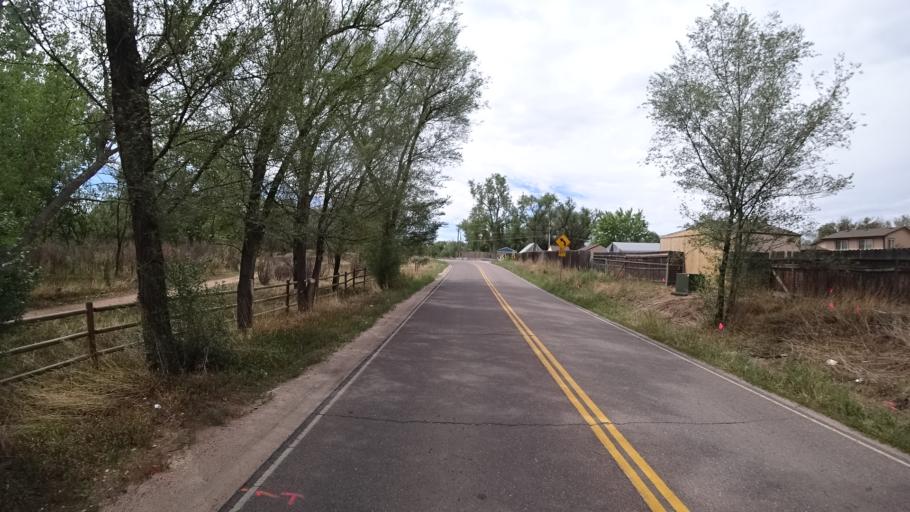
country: US
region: Colorado
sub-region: El Paso County
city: Fountain
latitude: 38.6775
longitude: -104.7012
